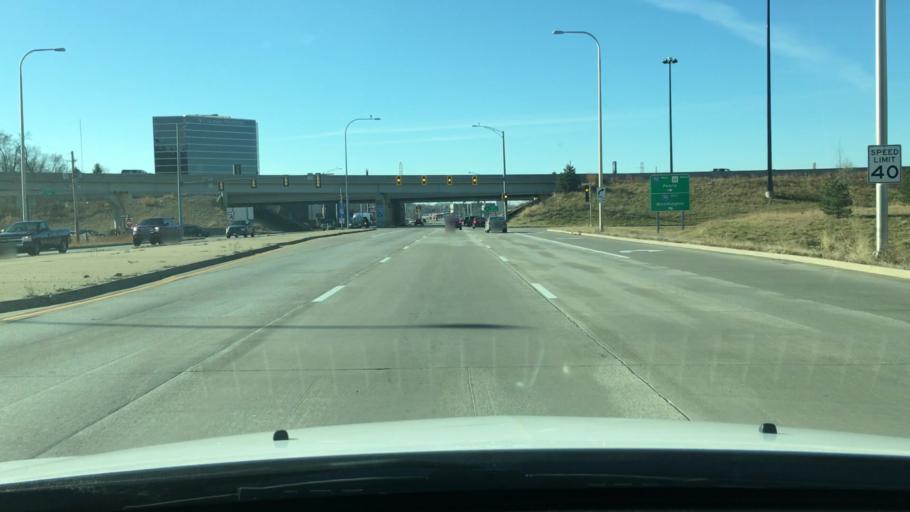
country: US
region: Illinois
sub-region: Tazewell County
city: East Peoria
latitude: 40.6713
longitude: -89.5723
